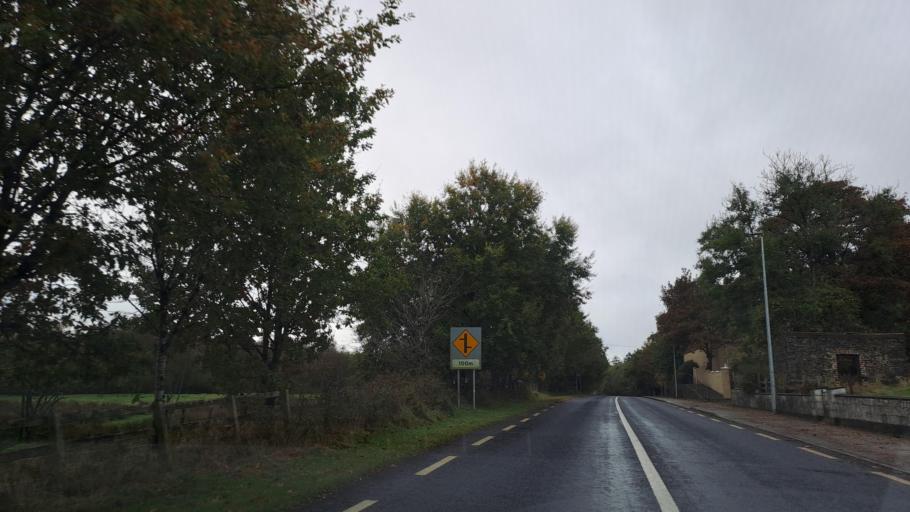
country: IE
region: Ulster
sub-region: An Cabhan
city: Bailieborough
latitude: 53.9096
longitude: -6.9760
